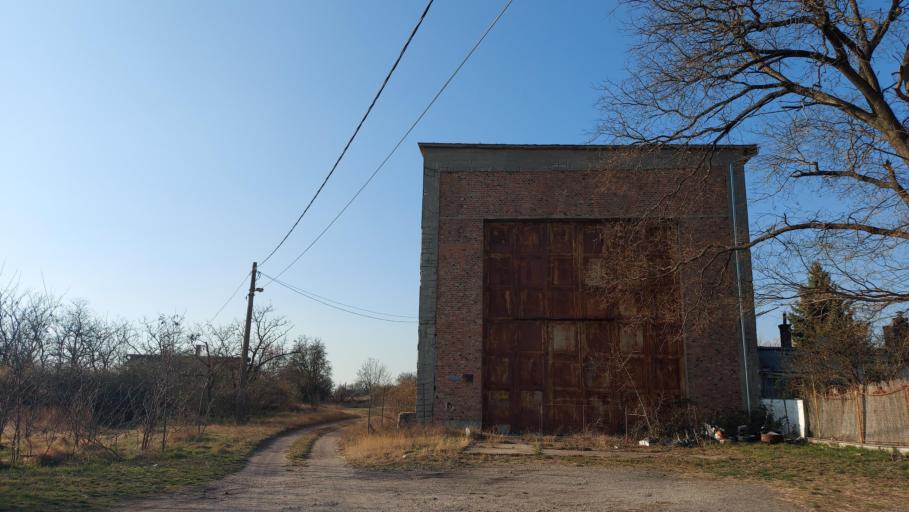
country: HU
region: Pest
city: Diosd
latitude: 47.4292
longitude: 18.9556
